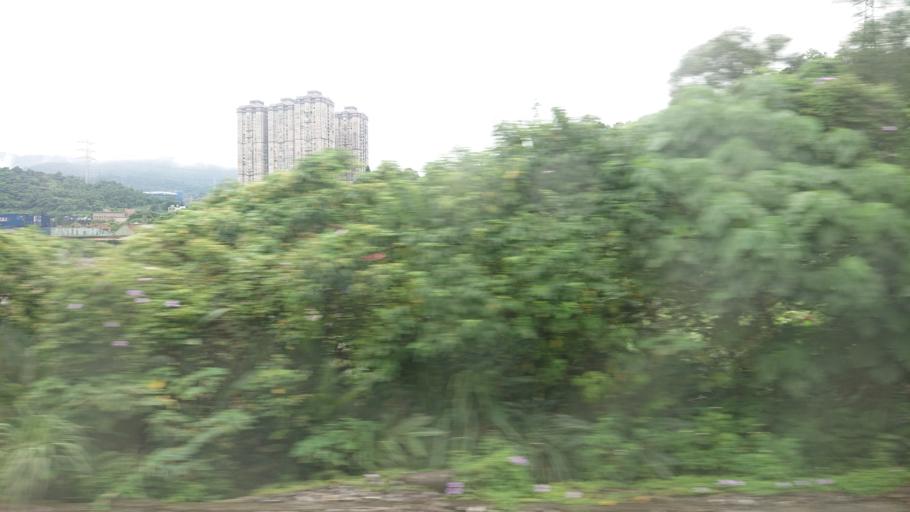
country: TW
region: Taiwan
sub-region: Keelung
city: Keelung
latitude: 25.0808
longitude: 121.6831
